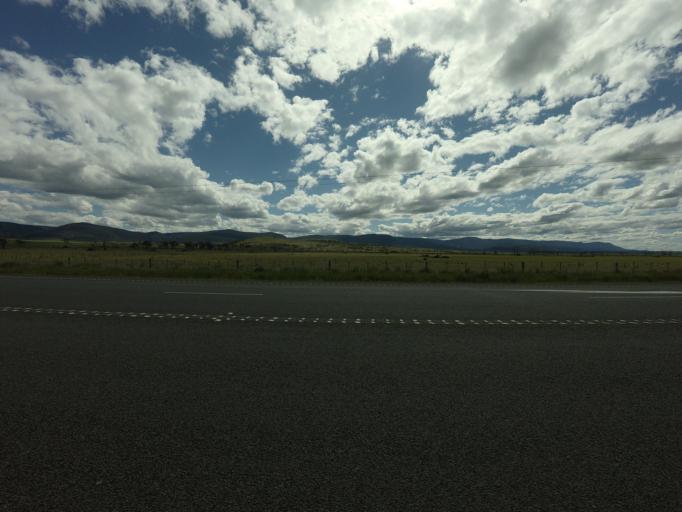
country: AU
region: Tasmania
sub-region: Brighton
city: Bridgewater
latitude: -42.1606
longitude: 147.4011
